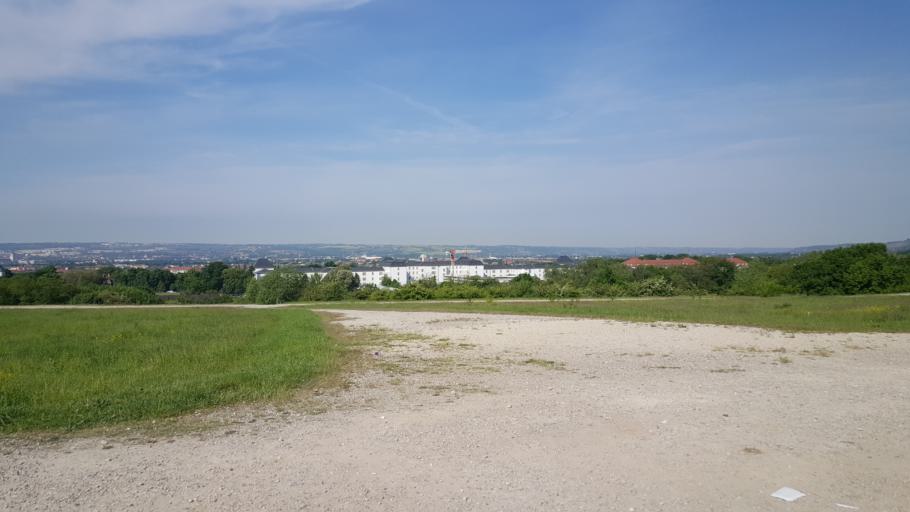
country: DE
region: Saxony
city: Albertstadt
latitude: 51.0854
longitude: 13.7542
